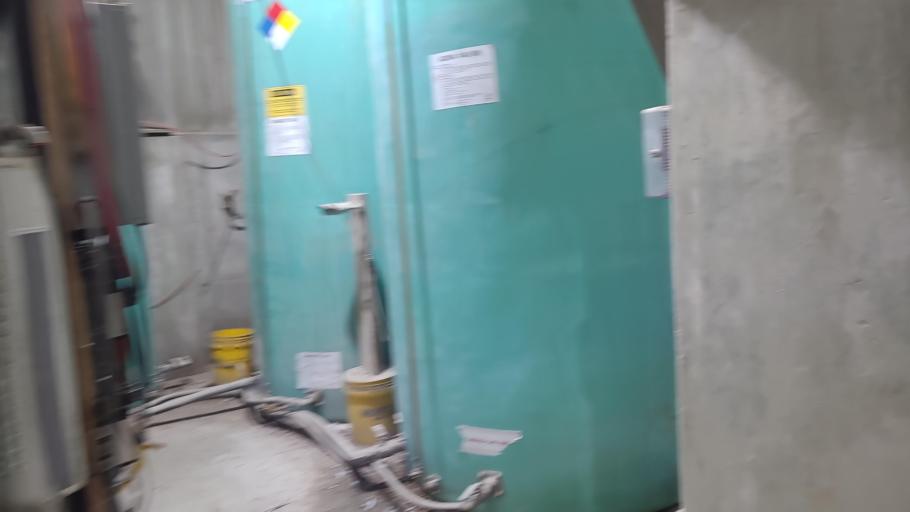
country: US
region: Kansas
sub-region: Douglas County
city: Lawrence
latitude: 38.9397
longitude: -95.1890
